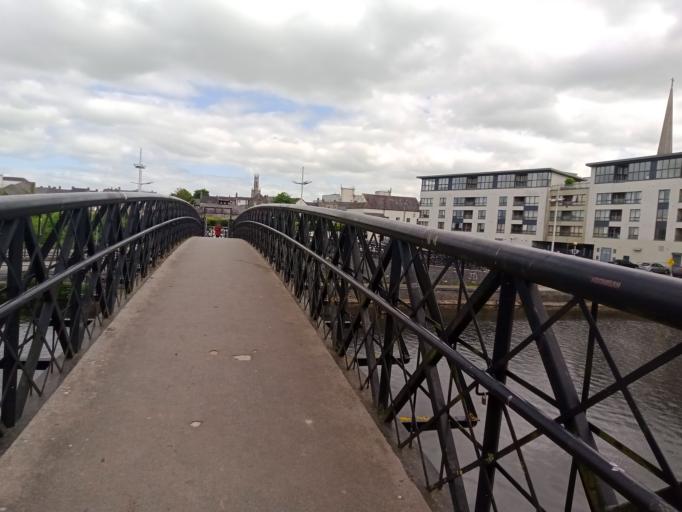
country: IE
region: Leinster
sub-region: County Carlow
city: Carlow
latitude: 52.8386
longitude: -6.9348
